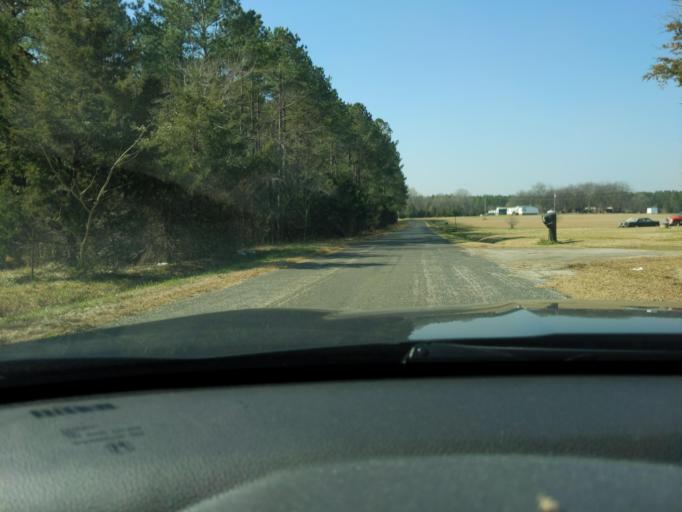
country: US
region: South Carolina
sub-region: Abbeville County
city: Calhoun Falls
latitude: 34.0861
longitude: -82.5549
